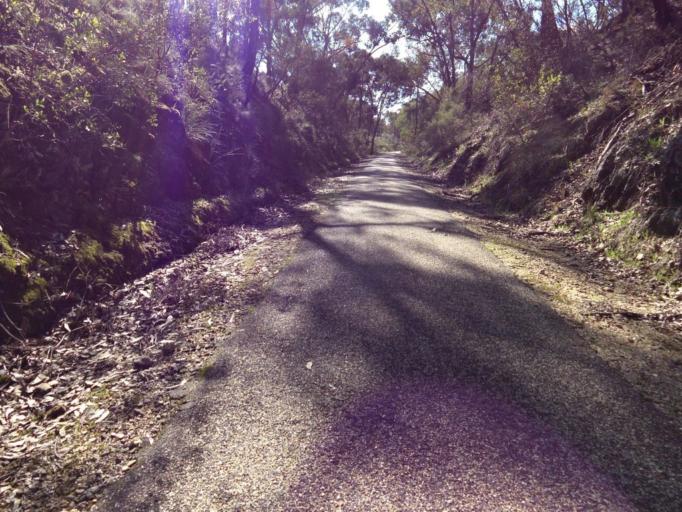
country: AU
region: Victoria
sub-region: Wangaratta
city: Wangaratta
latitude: -36.4076
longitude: 146.6177
